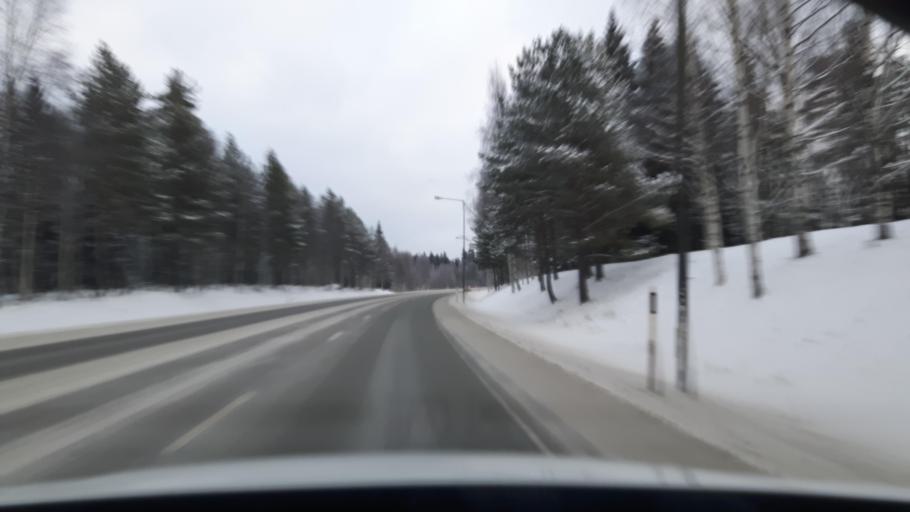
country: SE
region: Vaesterbotten
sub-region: Umea Kommun
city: Umea
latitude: 63.8447
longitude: 20.2793
